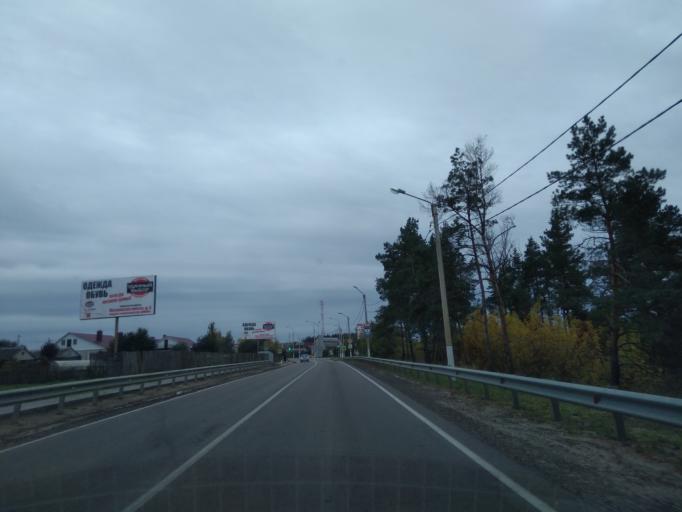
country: RU
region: Lipetsk
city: Zadonsk
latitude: 52.3842
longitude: 38.9371
